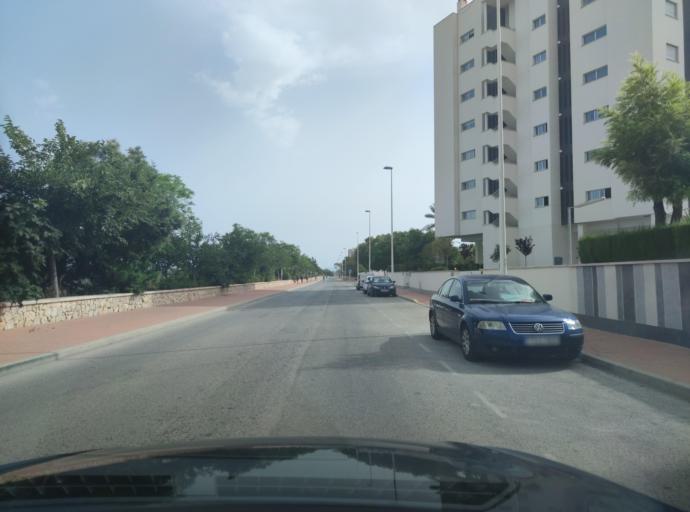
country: ES
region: Valencia
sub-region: Provincia de Alicante
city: Guardamar del Segura
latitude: 38.1038
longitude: -0.6554
